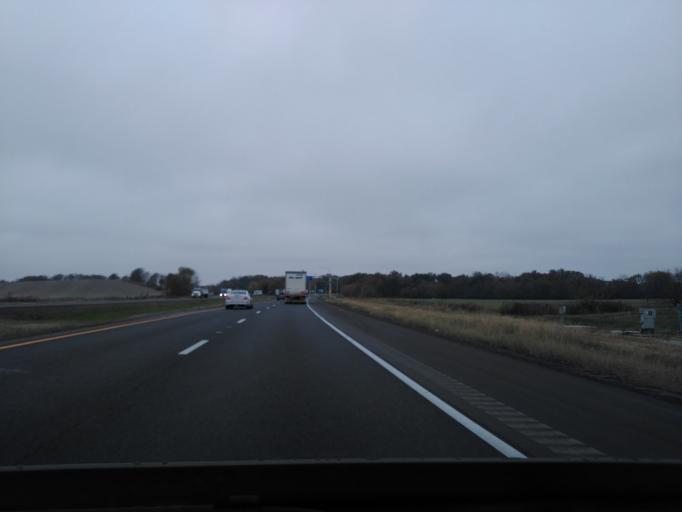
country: US
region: Illinois
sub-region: Madison County
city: Highland
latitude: 38.7871
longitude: -89.6811
